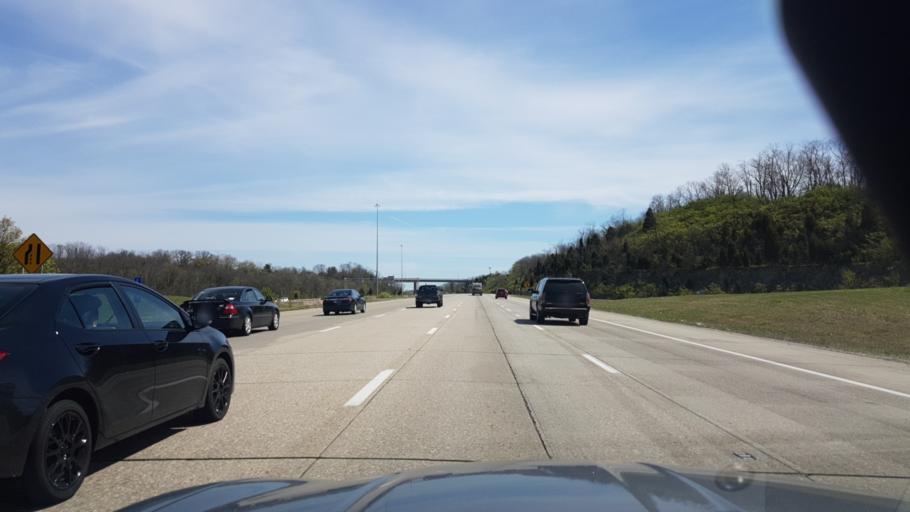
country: US
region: Kentucky
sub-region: Campbell County
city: Highland Heights
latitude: 39.0468
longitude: -84.4573
